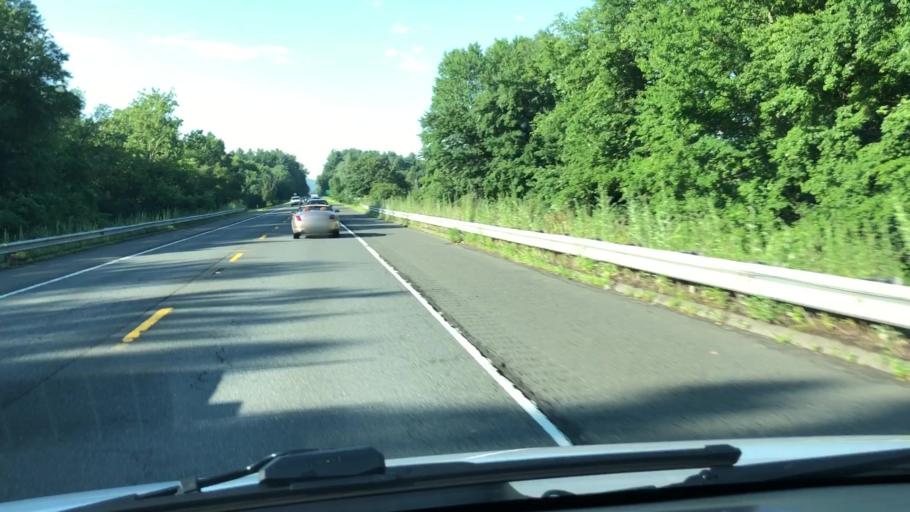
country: US
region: Massachusetts
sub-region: Hampshire County
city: North Amherst
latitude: 42.4054
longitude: -72.5386
